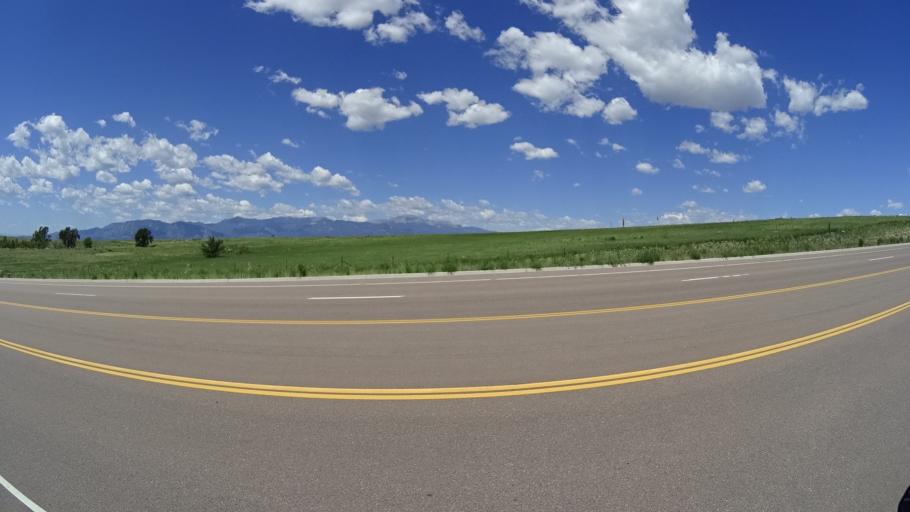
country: US
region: Colorado
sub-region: El Paso County
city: Cimarron Hills
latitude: 38.8486
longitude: -104.6825
